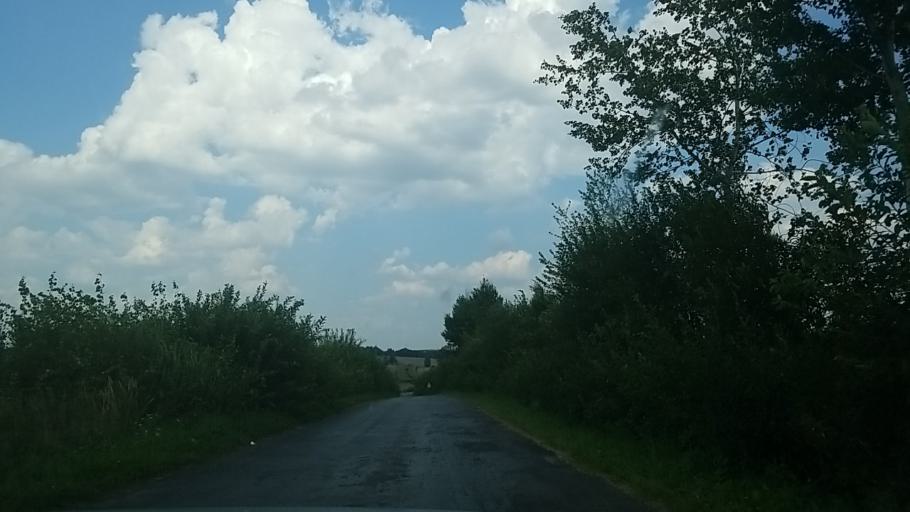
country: PL
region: Lublin Voivodeship
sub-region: Powiat bilgorajski
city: Goraj
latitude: 50.7221
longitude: 22.6181
